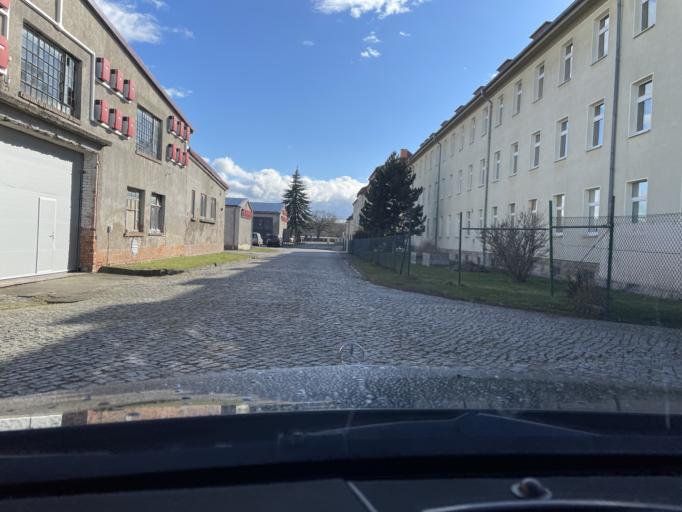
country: DE
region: Thuringia
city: Muehlhausen
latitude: 51.2183
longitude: 10.4624
